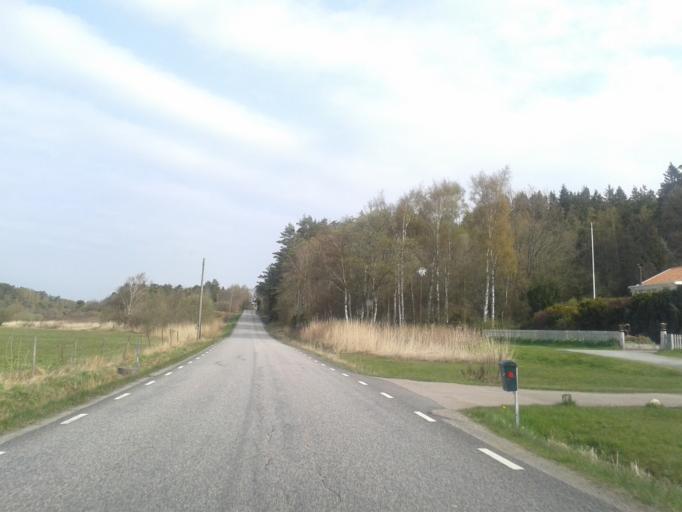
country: SE
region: Vaestra Goetaland
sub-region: Kungalvs Kommun
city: Kode
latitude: 57.9018
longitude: 11.8055
